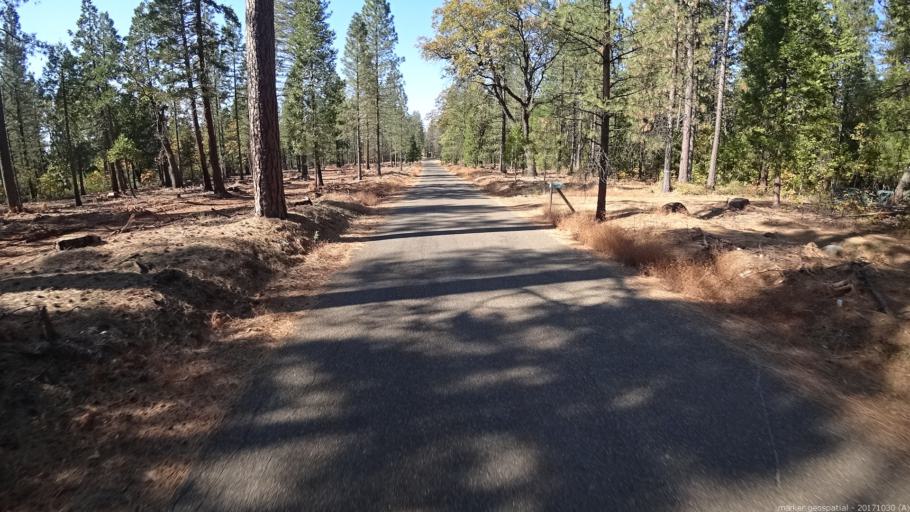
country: US
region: California
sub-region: Shasta County
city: Shingletown
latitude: 40.6103
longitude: -121.8734
